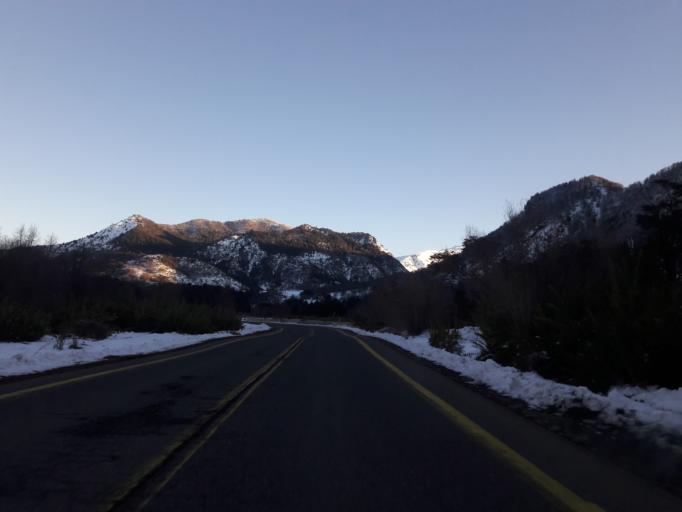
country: CL
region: Araucania
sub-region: Provincia de Cautin
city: Vilcun
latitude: -38.4959
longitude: -71.5209
